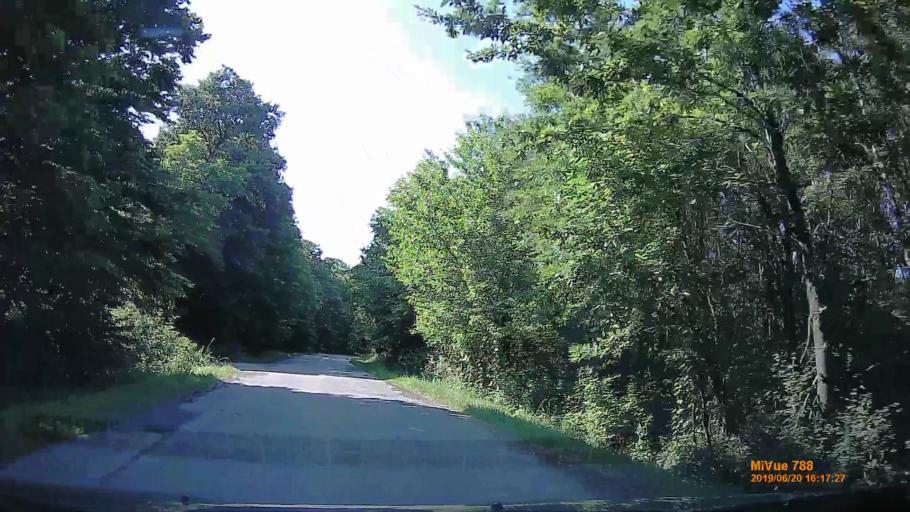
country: HU
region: Baranya
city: Buekkoesd
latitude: 46.1041
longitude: 18.0603
